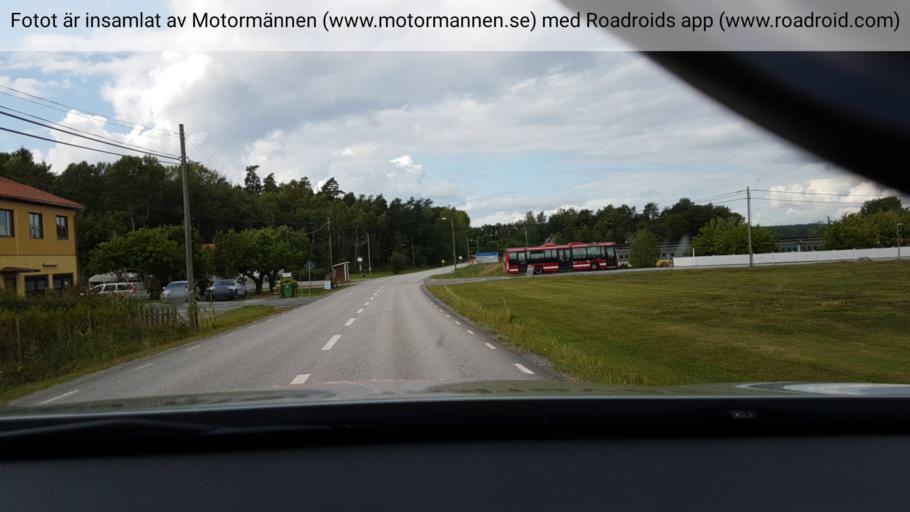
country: SE
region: Stockholm
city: Stenhamra
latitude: 59.3810
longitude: 17.6887
